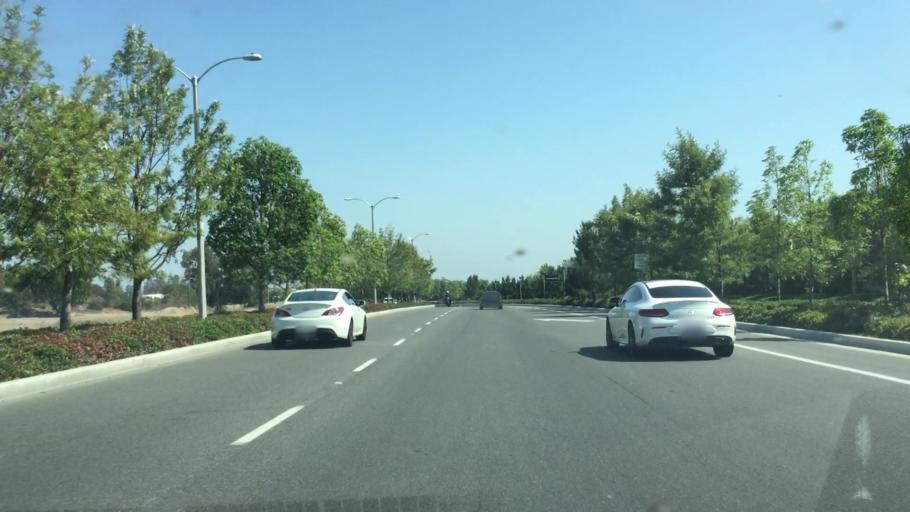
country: US
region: California
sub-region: Orange County
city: North Tustin
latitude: 33.7149
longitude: -117.7396
